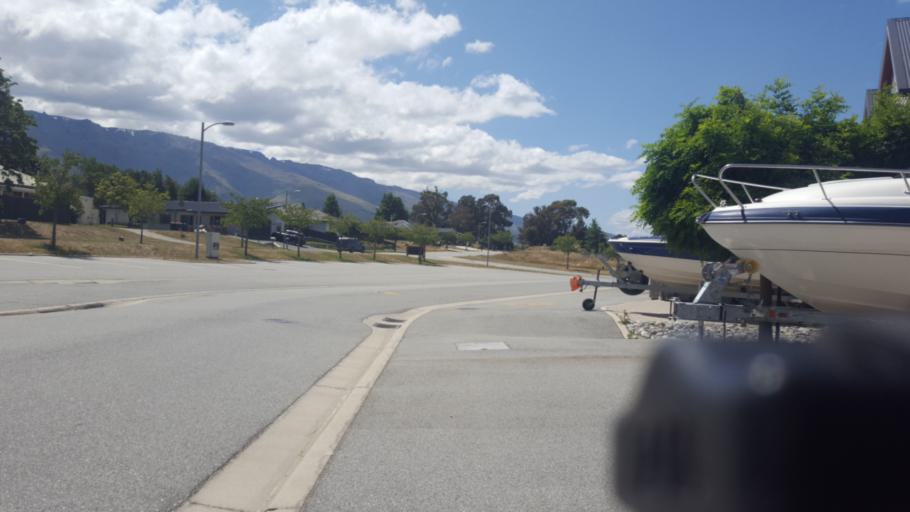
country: NZ
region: Otago
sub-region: Queenstown-Lakes District
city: Wanaka
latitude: -44.9802
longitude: 169.2359
